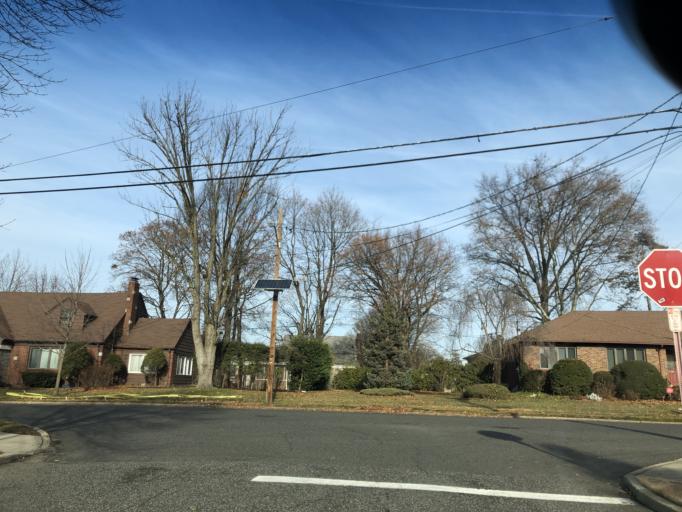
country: US
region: New Jersey
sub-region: Bergen County
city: Fair Lawn
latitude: 40.9278
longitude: -74.1287
